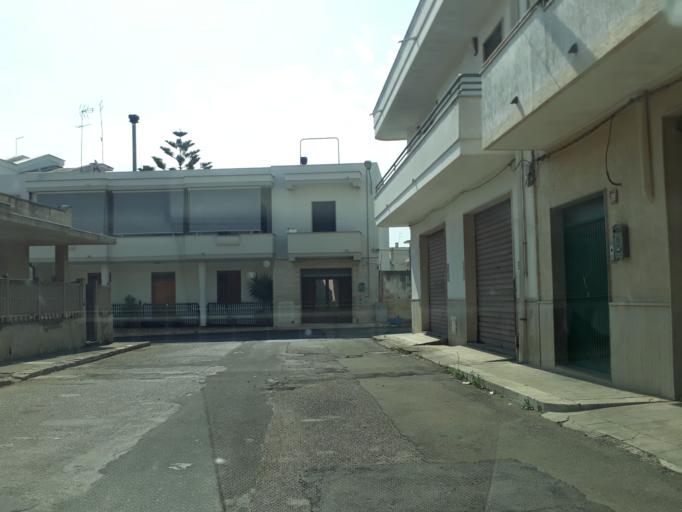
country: IT
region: Apulia
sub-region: Provincia di Brindisi
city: Carovigno
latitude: 40.7014
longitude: 17.6669
